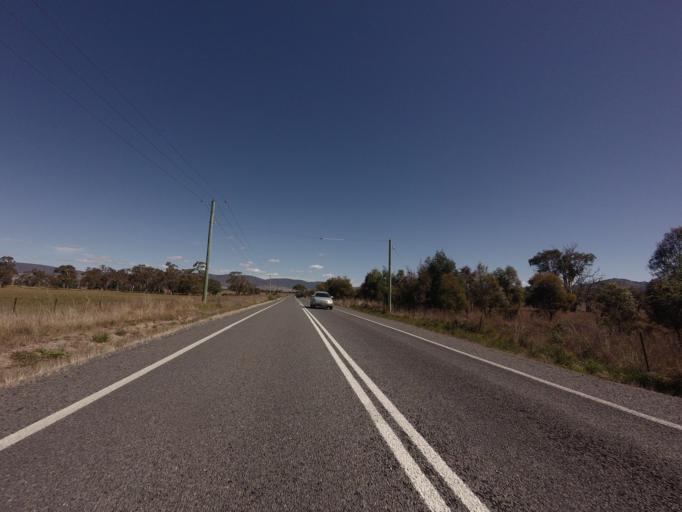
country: AU
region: Tasmania
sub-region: Northern Midlands
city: Evandale
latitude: -41.7723
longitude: 147.7366
